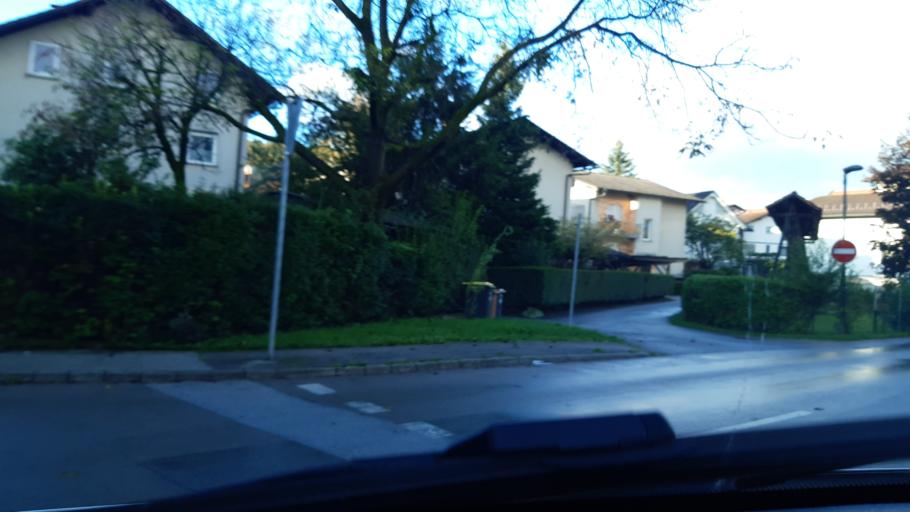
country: SI
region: Ljubljana
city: Ljubljana
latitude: 46.0507
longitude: 14.5431
